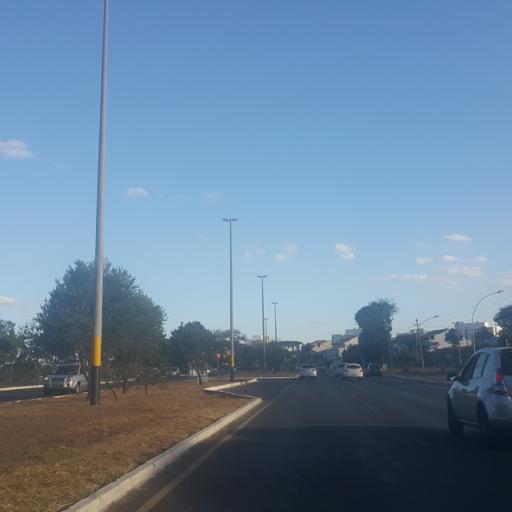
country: BR
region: Federal District
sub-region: Brasilia
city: Brasilia
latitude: -15.8323
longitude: -47.9747
